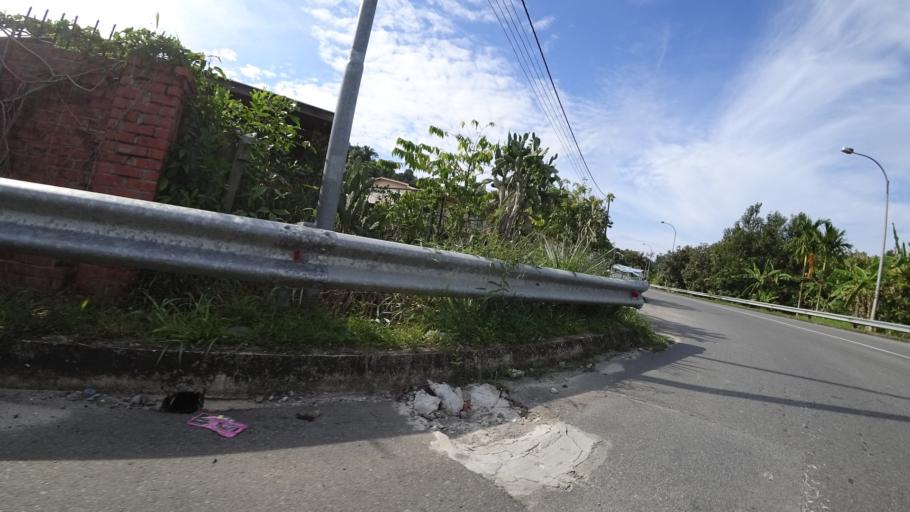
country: BN
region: Brunei and Muara
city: Bandar Seri Begawan
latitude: 4.8772
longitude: 114.8026
